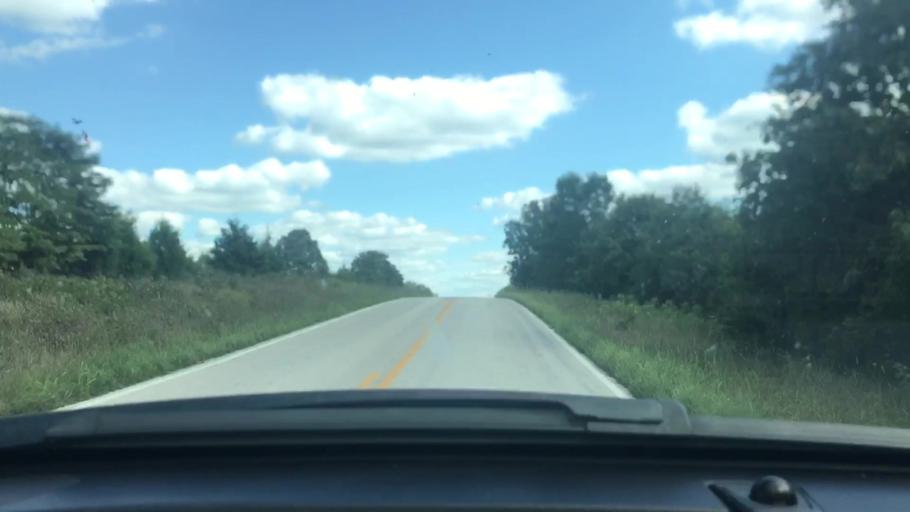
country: US
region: Missouri
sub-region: Wright County
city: Hartville
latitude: 37.3896
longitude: -92.4475
